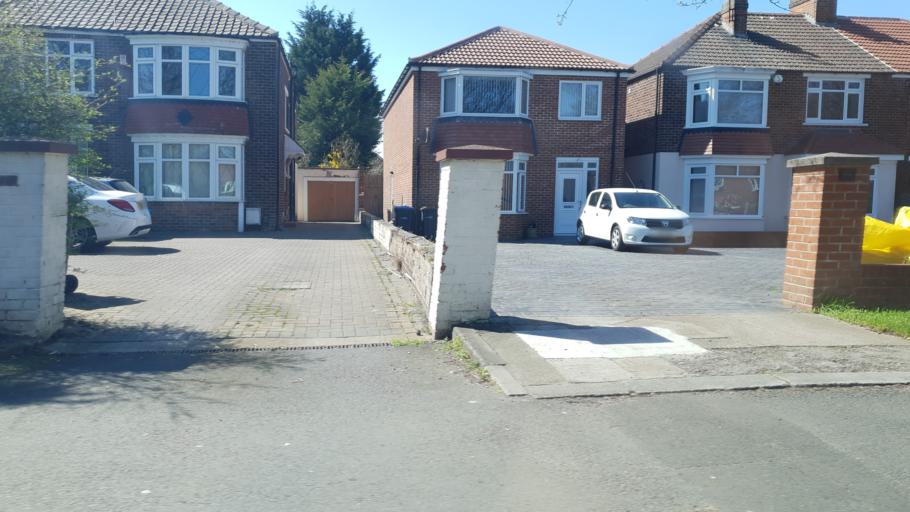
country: GB
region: England
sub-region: Middlesbrough
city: Nunthorpe
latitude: 54.5450
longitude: -1.2143
